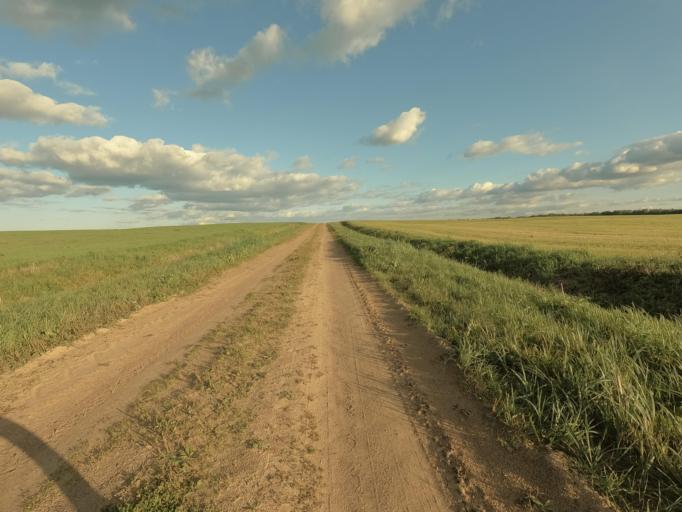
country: RU
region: Leningrad
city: Imeni Sverdlova
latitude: 59.8654
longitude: 30.7369
